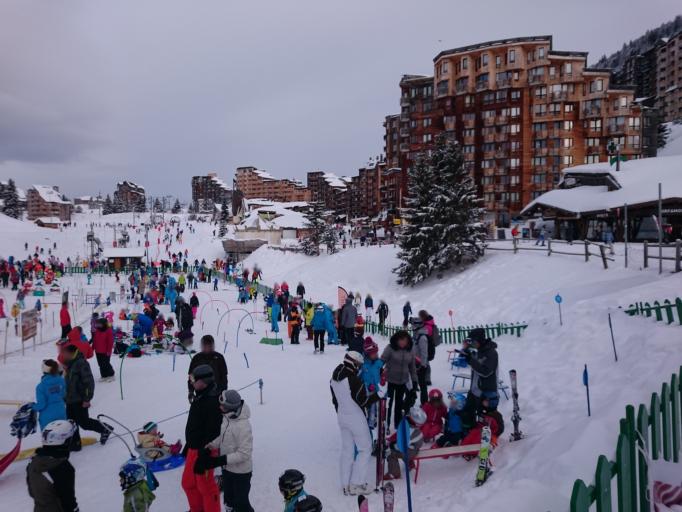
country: FR
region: Rhone-Alpes
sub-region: Departement de la Haute-Savoie
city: Morzine
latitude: 46.1902
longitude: 6.7774
